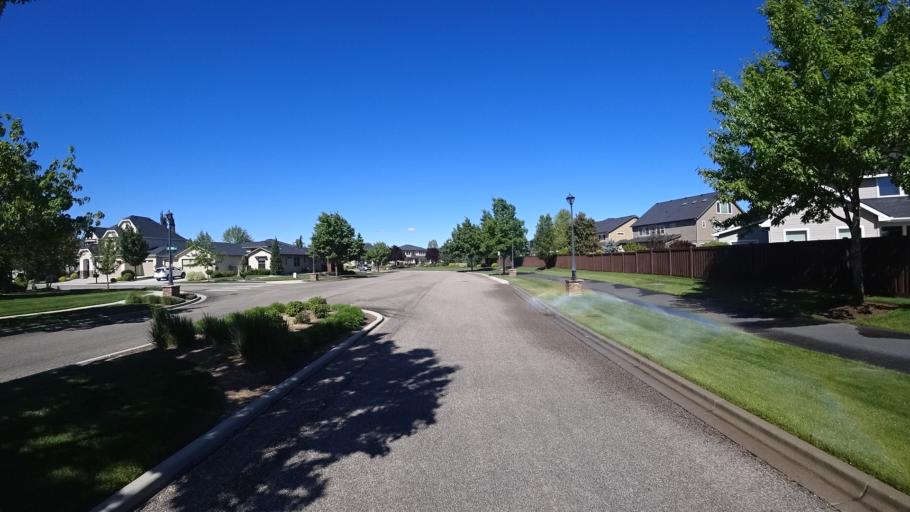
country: US
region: Idaho
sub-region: Ada County
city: Meridian
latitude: 43.6555
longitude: -116.3960
